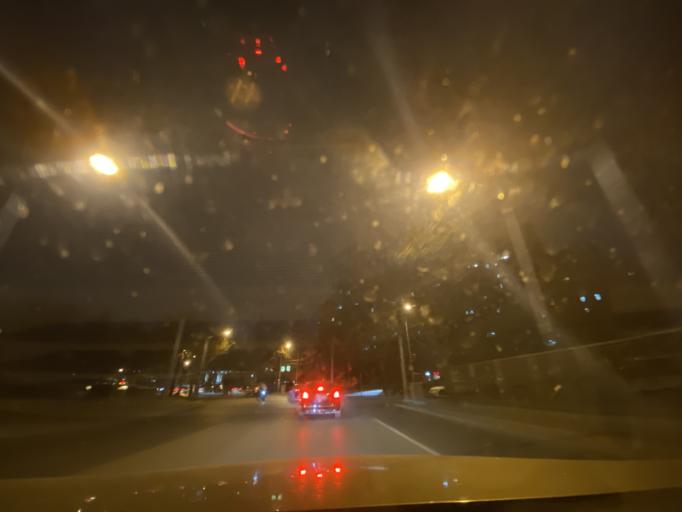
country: CN
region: Beijing
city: Baizhifang
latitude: 39.8991
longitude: 116.3425
